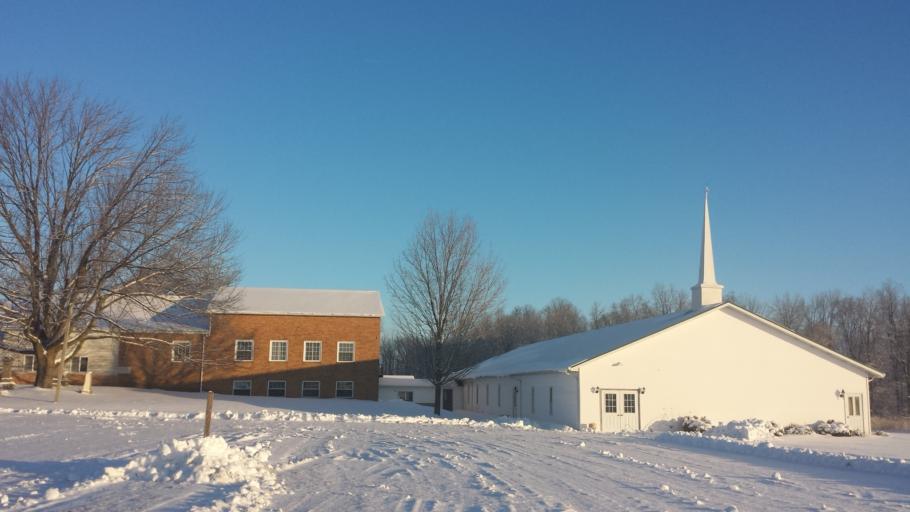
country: US
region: Ohio
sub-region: Ashland County
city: Ashland
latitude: 40.9158
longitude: -82.3874
